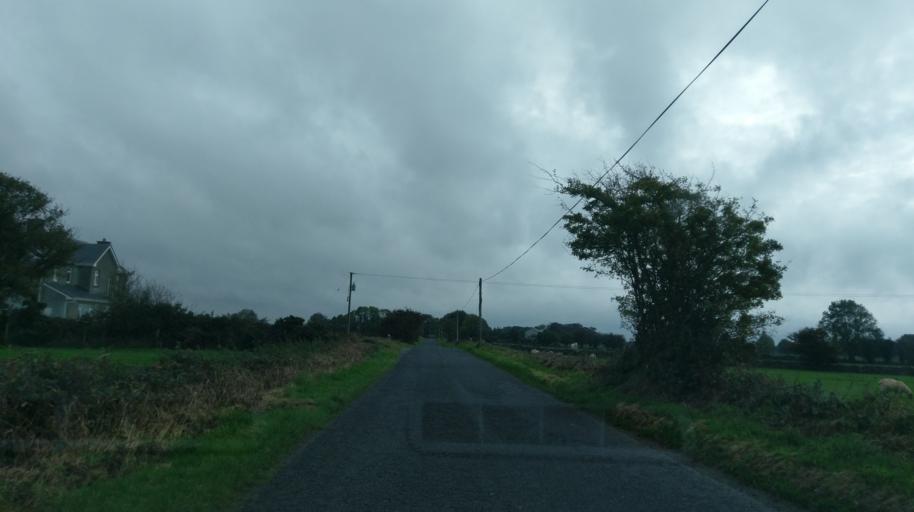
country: IE
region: Connaught
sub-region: County Galway
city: Athenry
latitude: 53.4558
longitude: -8.5960
